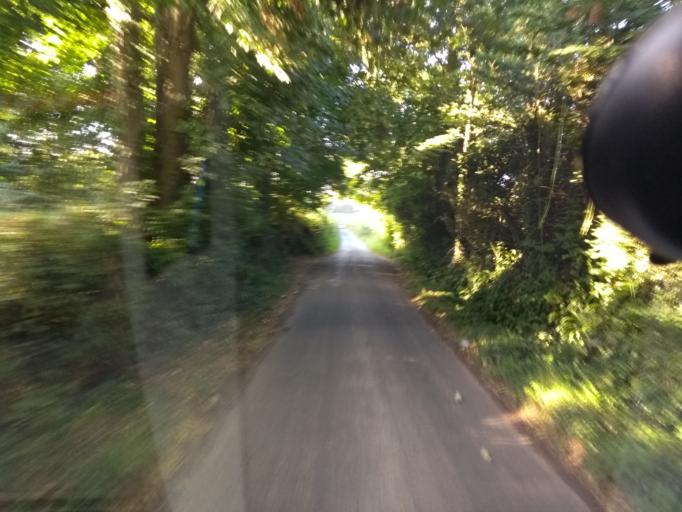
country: GB
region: England
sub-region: Somerset
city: South Petherton
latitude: 50.9764
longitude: -2.8106
